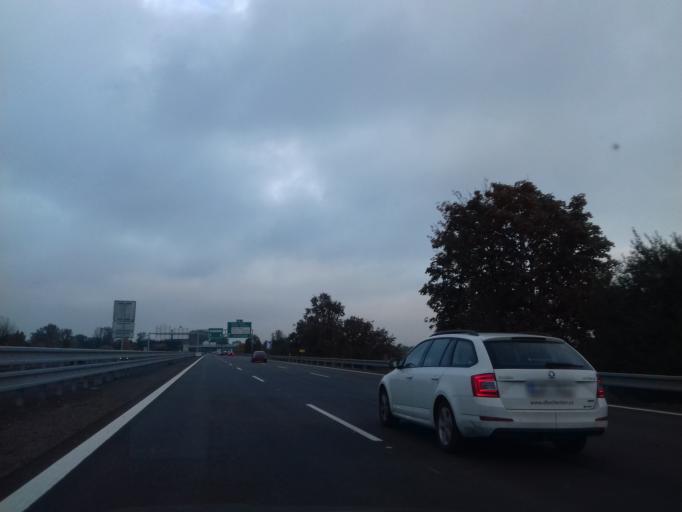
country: CZ
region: South Moravian
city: Modrice
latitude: 49.1411
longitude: 16.6342
